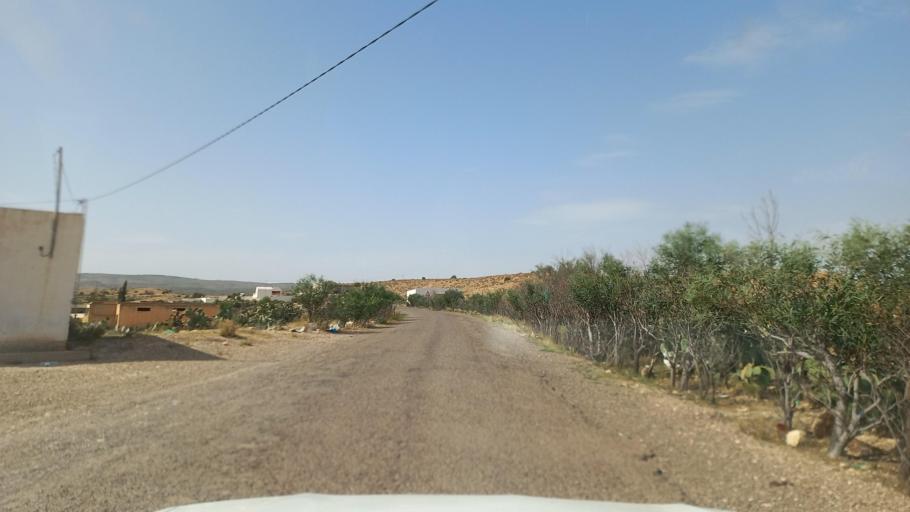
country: TN
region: Al Qasrayn
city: Kasserine
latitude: 35.3015
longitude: 8.9506
